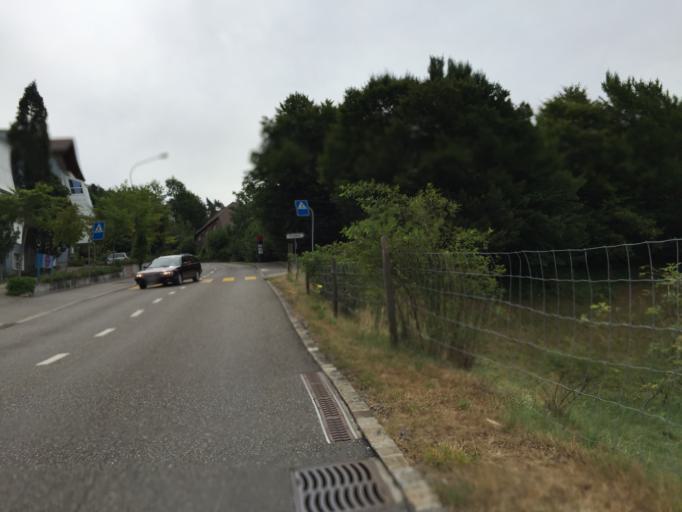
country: CH
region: Bern
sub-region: Bern-Mittelland District
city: Koniz
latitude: 46.9207
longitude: 7.4192
